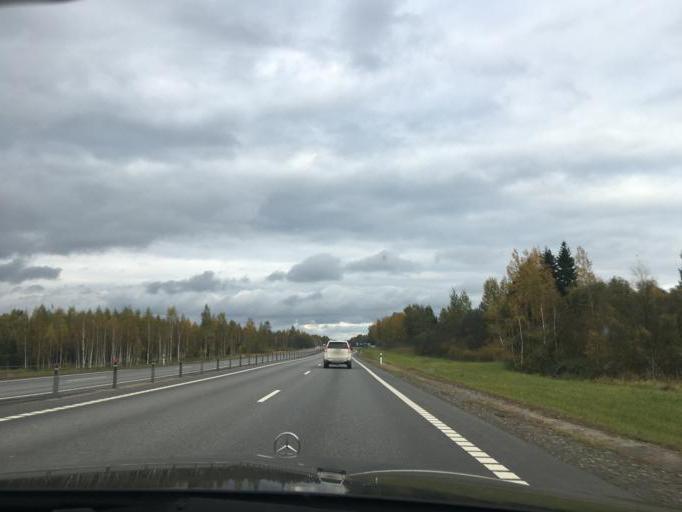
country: BY
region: Vitebsk
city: Dubrowna
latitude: 54.6894
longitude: 30.8979
